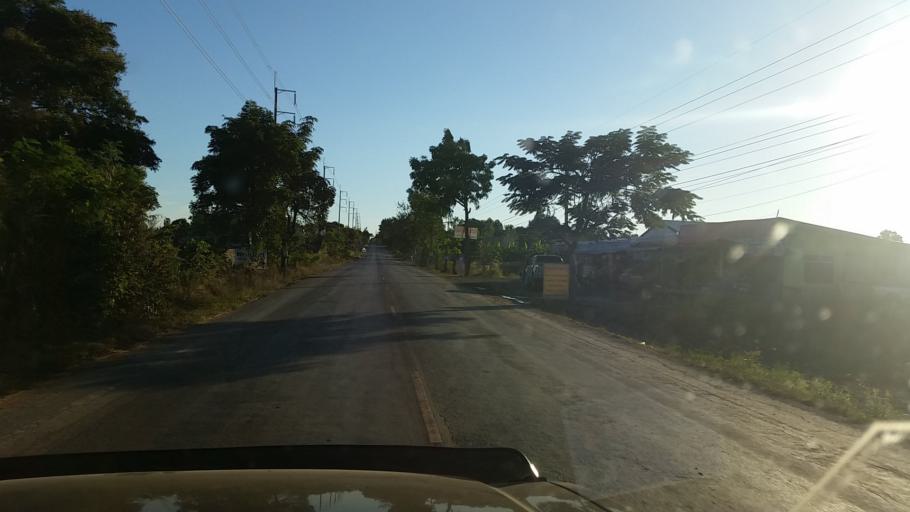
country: TH
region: Chaiyaphum
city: Nong Bua Rawe
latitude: 15.7258
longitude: 101.7451
